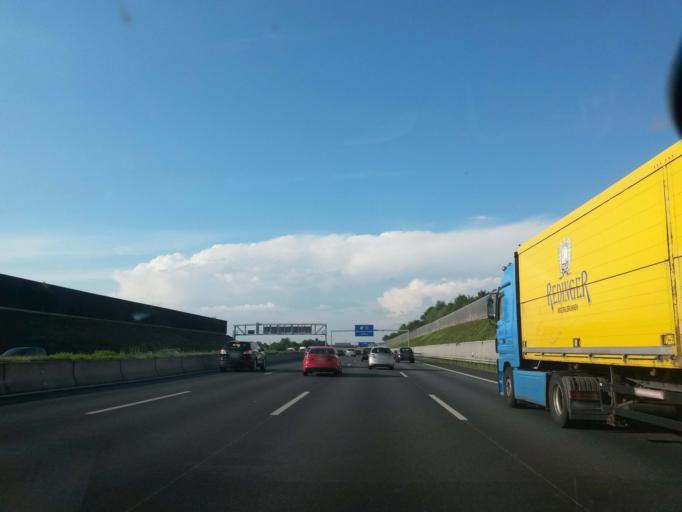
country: DE
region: Bavaria
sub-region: Upper Bavaria
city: Garching bei Munchen
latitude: 48.2500
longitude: 11.6439
